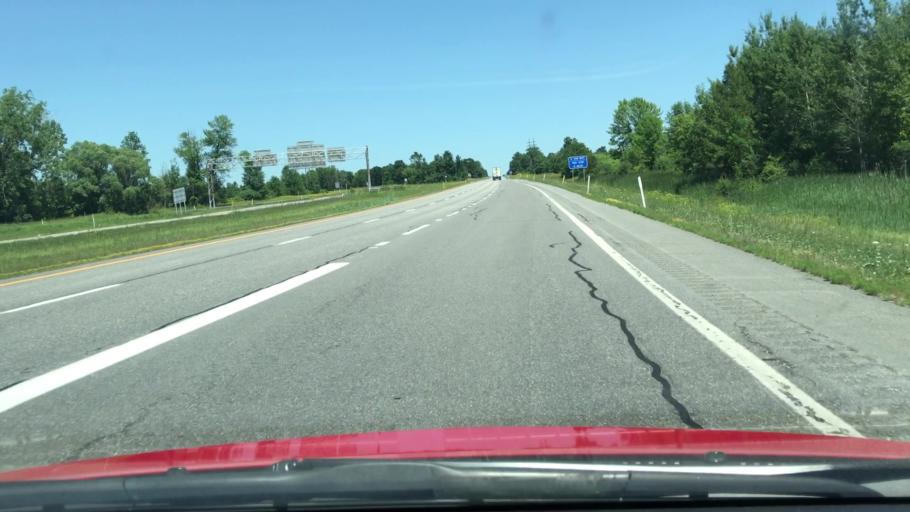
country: US
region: New York
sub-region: Clinton County
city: Plattsburgh
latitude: 44.7310
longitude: -73.4380
